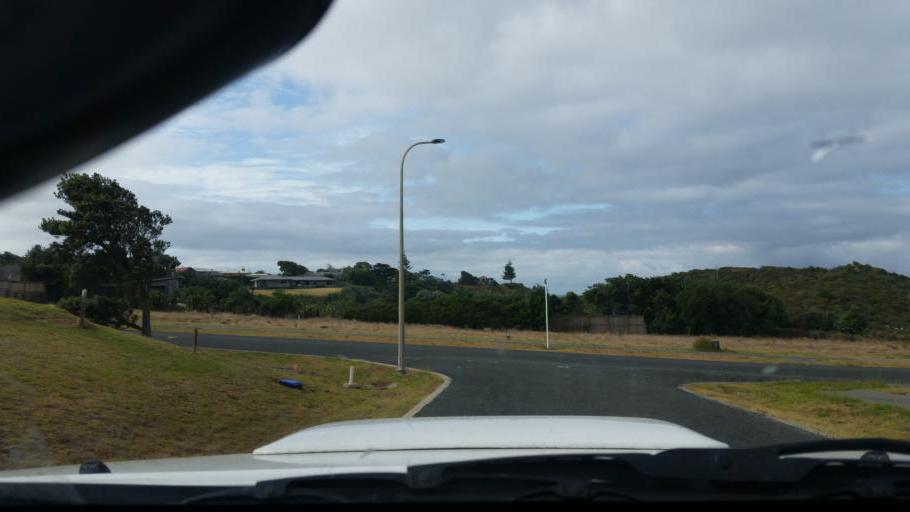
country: NZ
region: Northland
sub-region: Kaipara District
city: Dargaville
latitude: -35.9480
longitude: 173.7447
